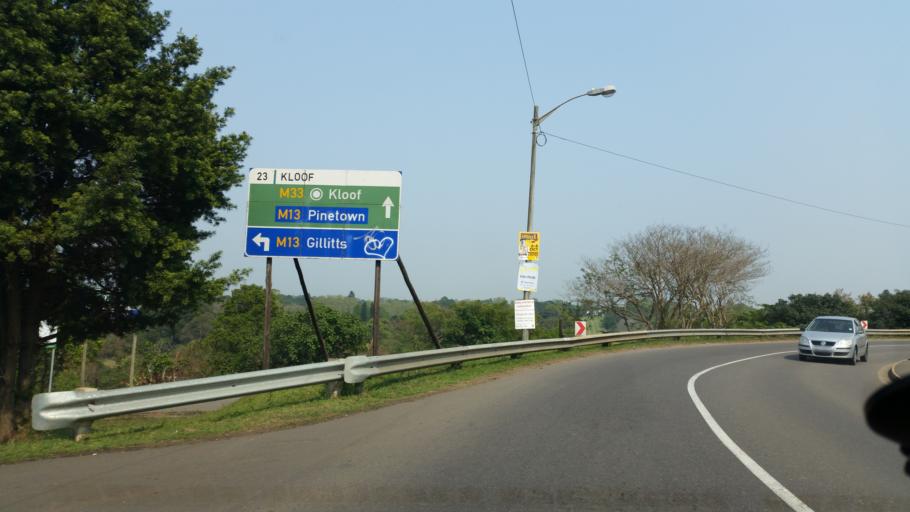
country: ZA
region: KwaZulu-Natal
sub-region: eThekwini Metropolitan Municipality
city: Berea
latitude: -29.7950
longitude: 30.8343
